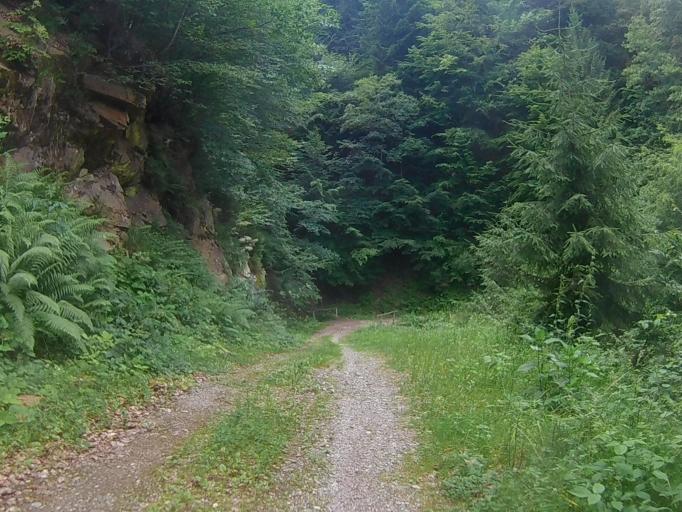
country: SI
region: Selnica ob Dravi
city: Selnica ob Dravi
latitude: 46.5184
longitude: 15.4852
